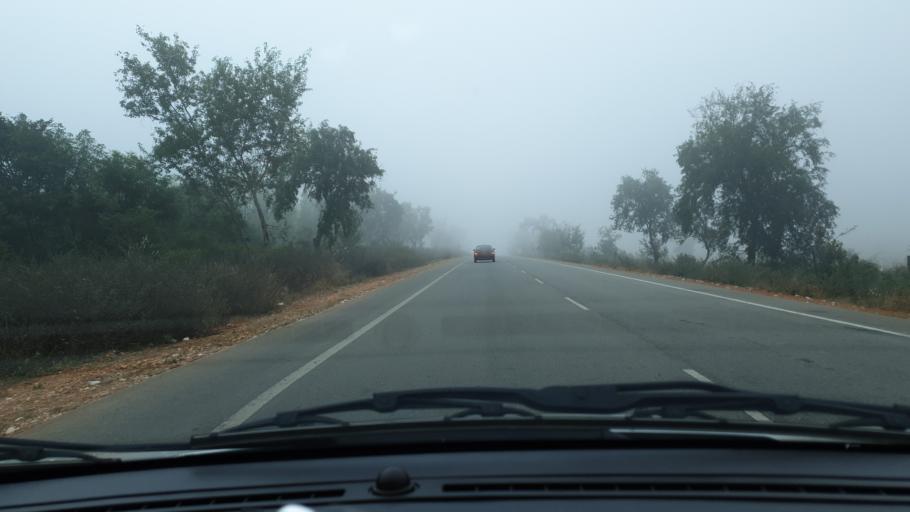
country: IN
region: Telangana
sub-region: Mahbubnagar
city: Nagar Karnul
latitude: 16.6580
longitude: 78.5765
